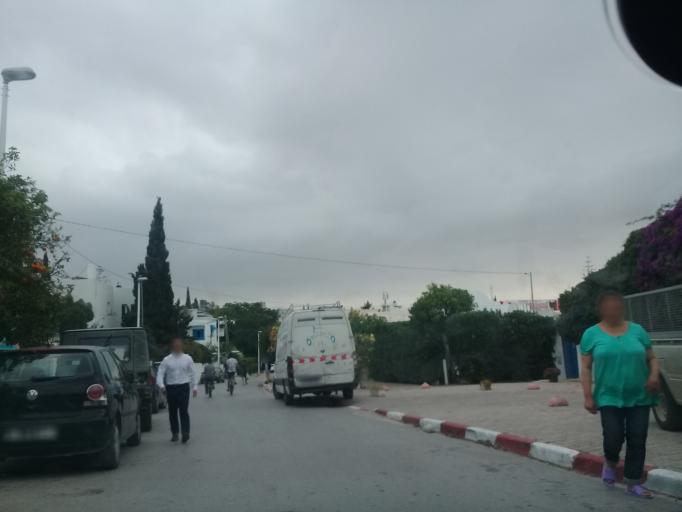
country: TN
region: Tunis
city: Sidi Bou Said
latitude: 36.8715
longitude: 10.3405
